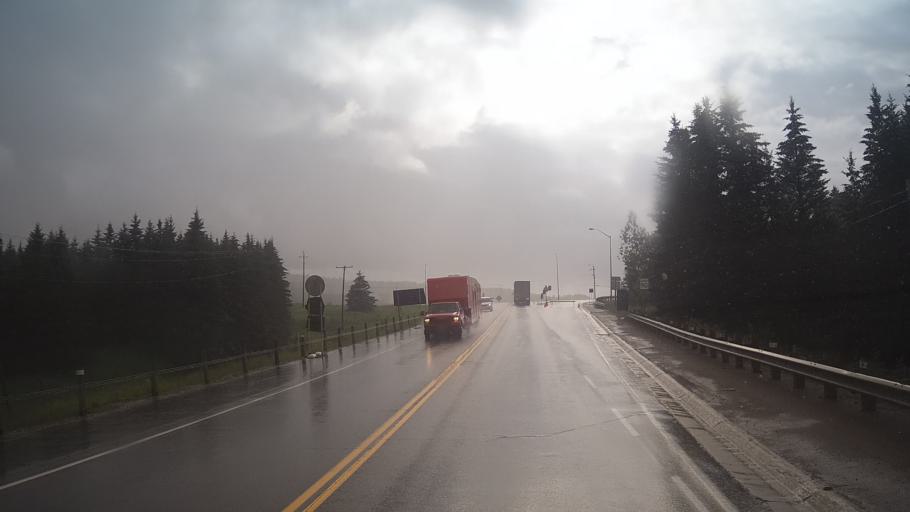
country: CA
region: Ontario
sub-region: Thunder Bay District
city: Thunder Bay
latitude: 48.5344
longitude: -89.6470
